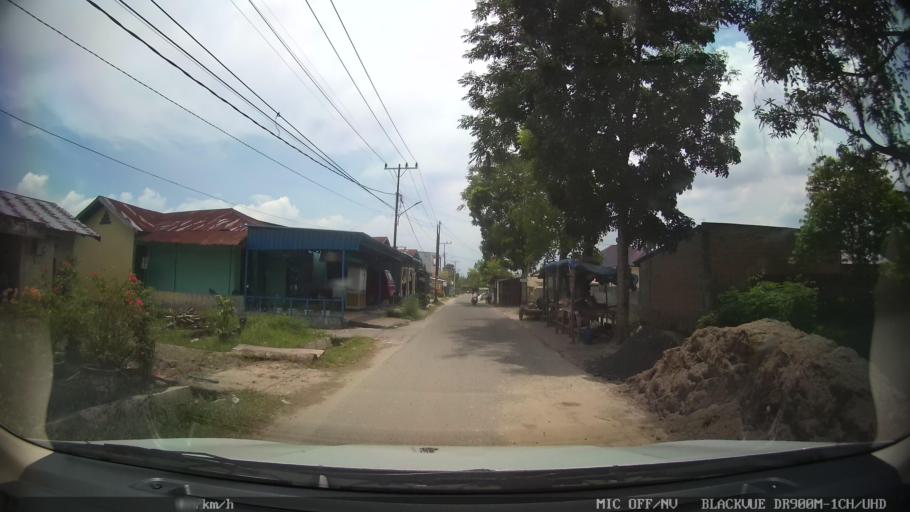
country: ID
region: North Sumatra
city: Binjai
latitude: 3.6208
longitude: 98.5057
